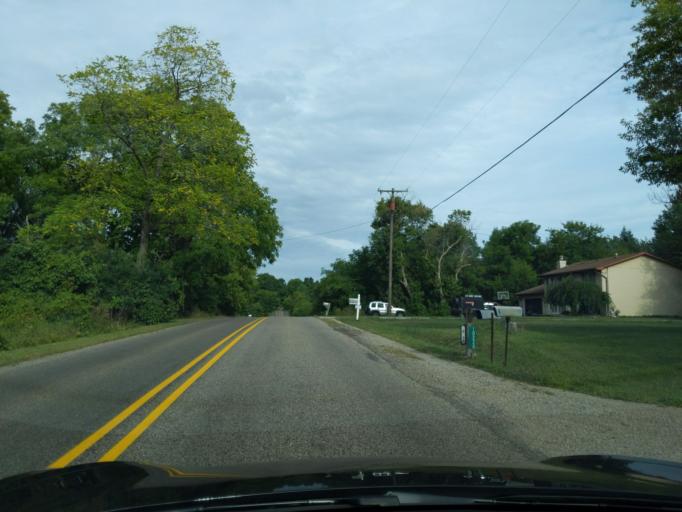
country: US
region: Michigan
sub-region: Eaton County
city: Dimondale
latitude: 42.6691
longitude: -84.6376
